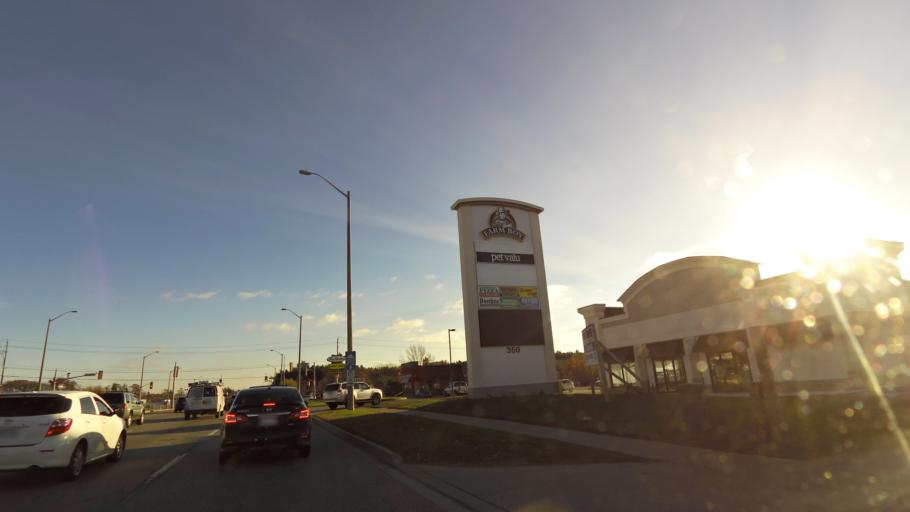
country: CA
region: Ontario
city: Cambridge
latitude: 43.3916
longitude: -80.3230
